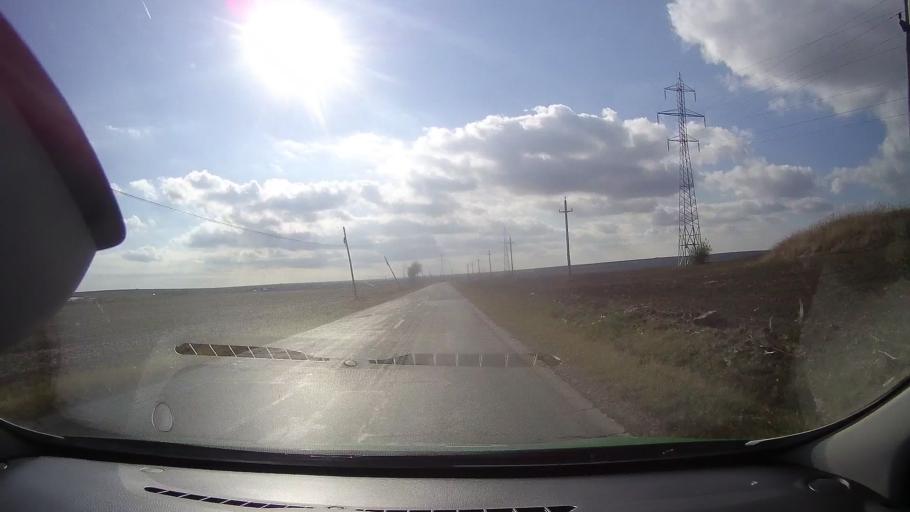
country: RO
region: Constanta
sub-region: Comuna Istria
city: Nuntasi
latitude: 44.5362
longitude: 28.6869
